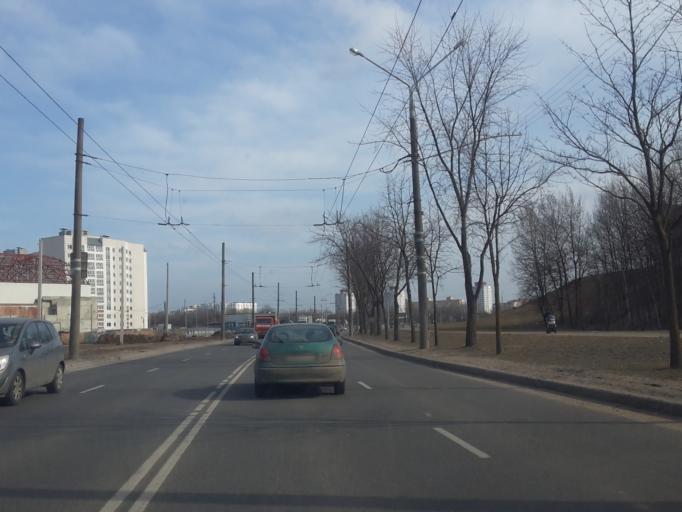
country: BY
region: Minsk
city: Novoye Medvezhino
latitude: 53.8921
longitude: 27.4588
